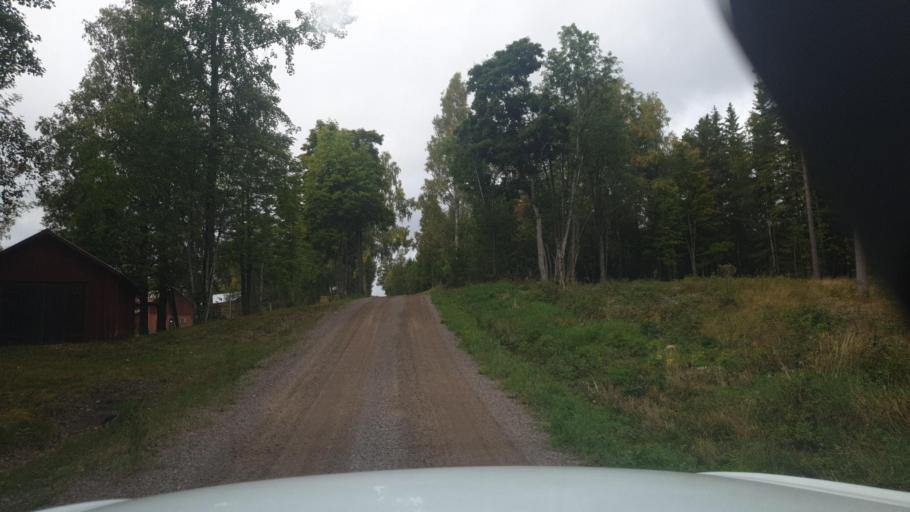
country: SE
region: Vaermland
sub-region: Torsby Kommun
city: Torsby
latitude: 59.9440
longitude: 12.7989
